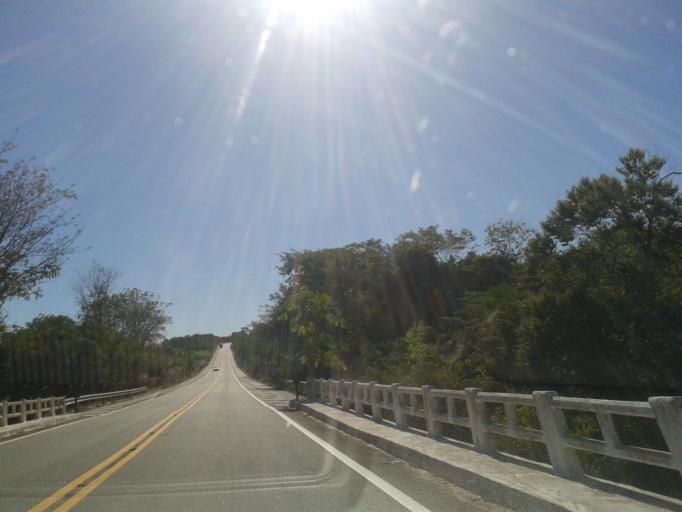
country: BR
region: Goias
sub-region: Goias
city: Goias
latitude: -15.7507
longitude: -50.1684
